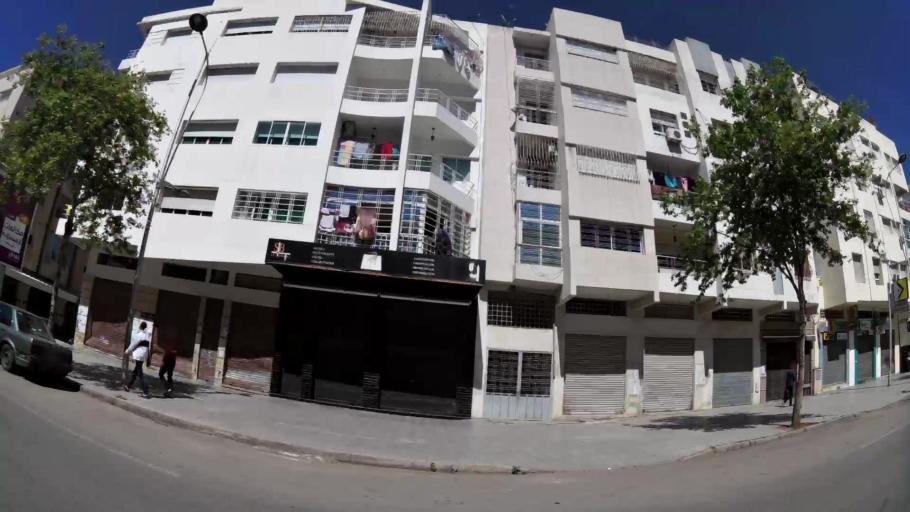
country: MA
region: Fes-Boulemane
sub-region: Fes
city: Fes
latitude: 34.0219
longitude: -4.9882
